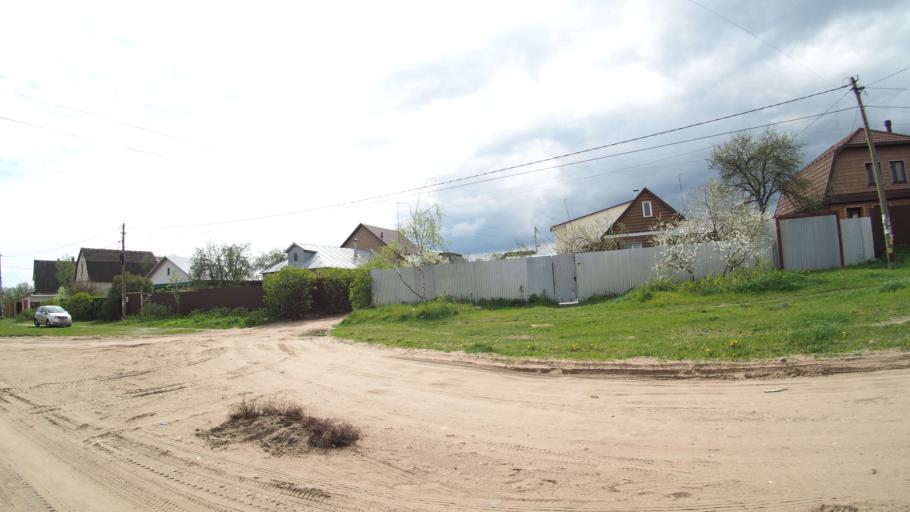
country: RU
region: Moskovskaya
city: Ramenskoye
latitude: 55.5501
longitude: 38.2365
